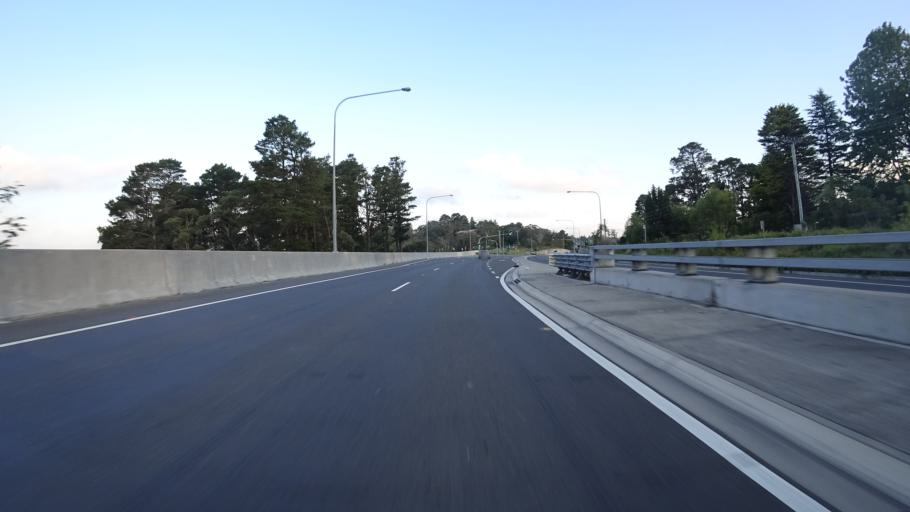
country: AU
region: New South Wales
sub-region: Blue Mountains Municipality
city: Lawson
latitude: -33.7158
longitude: 150.3823
